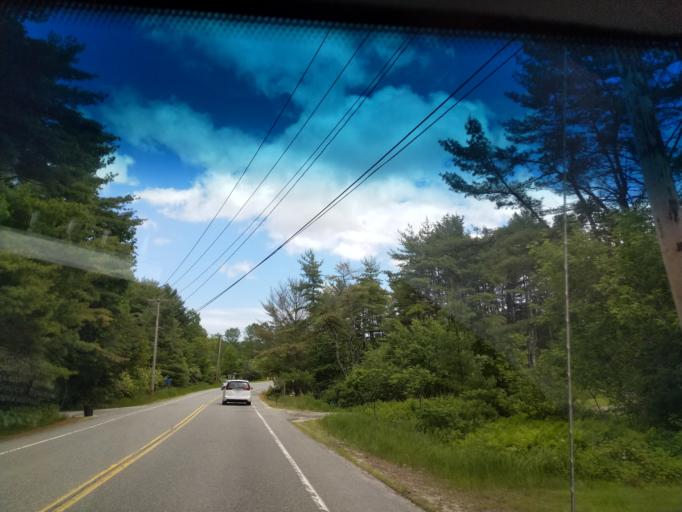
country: US
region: Maine
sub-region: Cumberland County
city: Falmouth
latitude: 43.7381
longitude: -70.2864
